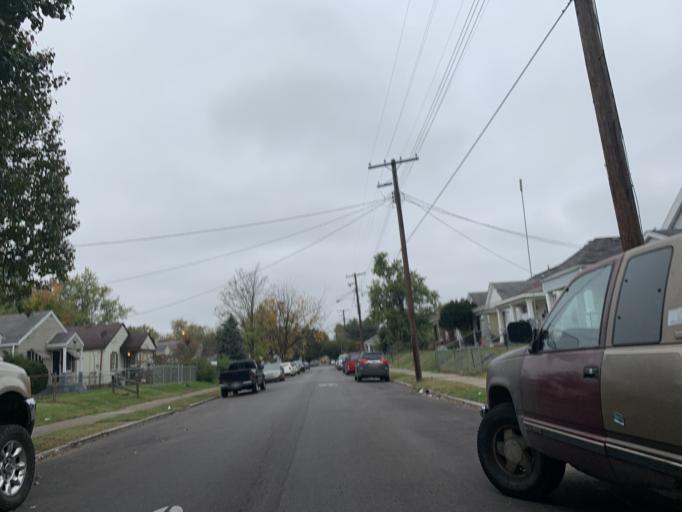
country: US
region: Indiana
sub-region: Floyd County
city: New Albany
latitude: 38.2623
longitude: -85.7957
